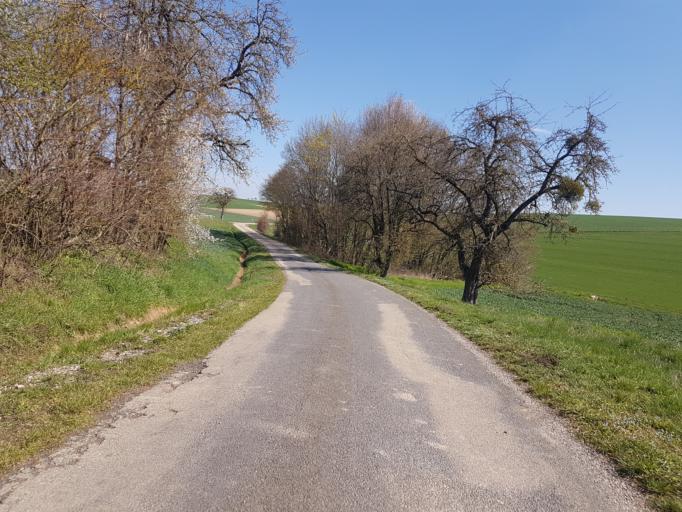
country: DE
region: Baden-Wuerttemberg
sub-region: Regierungsbezirk Stuttgart
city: Jagsthausen
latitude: 49.3506
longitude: 9.4936
